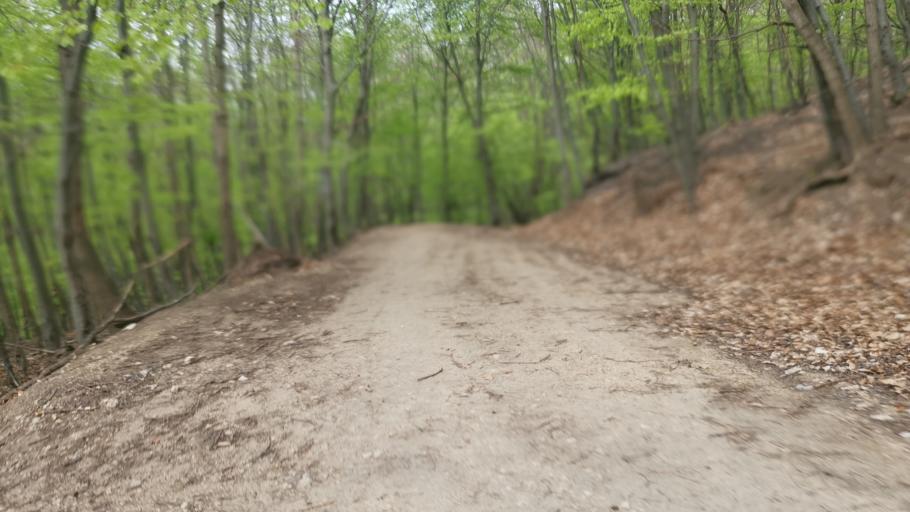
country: SK
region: Trnavsky
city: Smolenice
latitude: 48.5269
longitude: 17.3755
